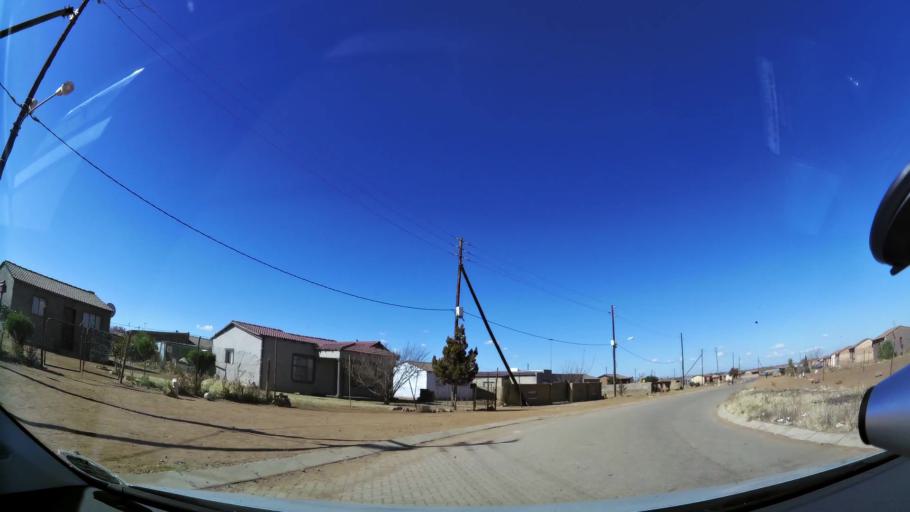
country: ZA
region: North-West
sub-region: Dr Kenneth Kaunda District Municipality
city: Klerksdorp
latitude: -26.8691
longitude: 26.5705
